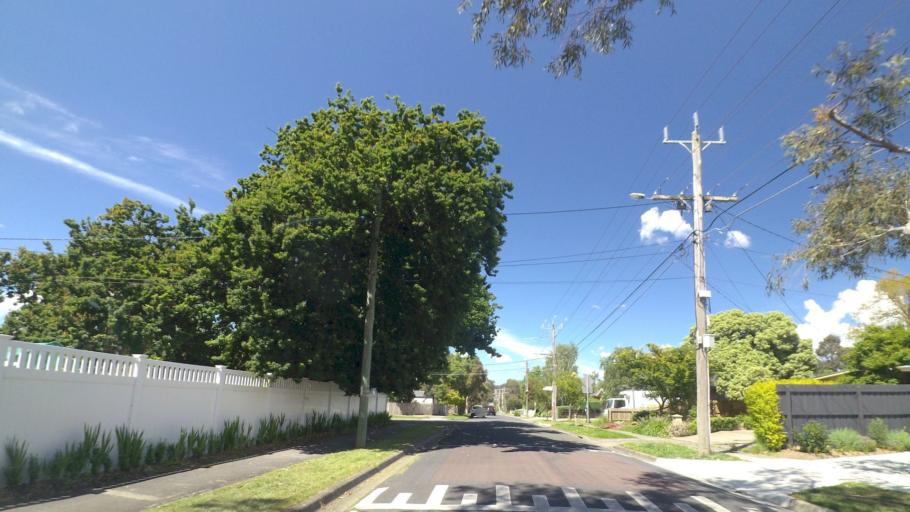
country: AU
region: Victoria
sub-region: Maroondah
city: Croydon South
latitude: -37.8200
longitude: 145.2751
